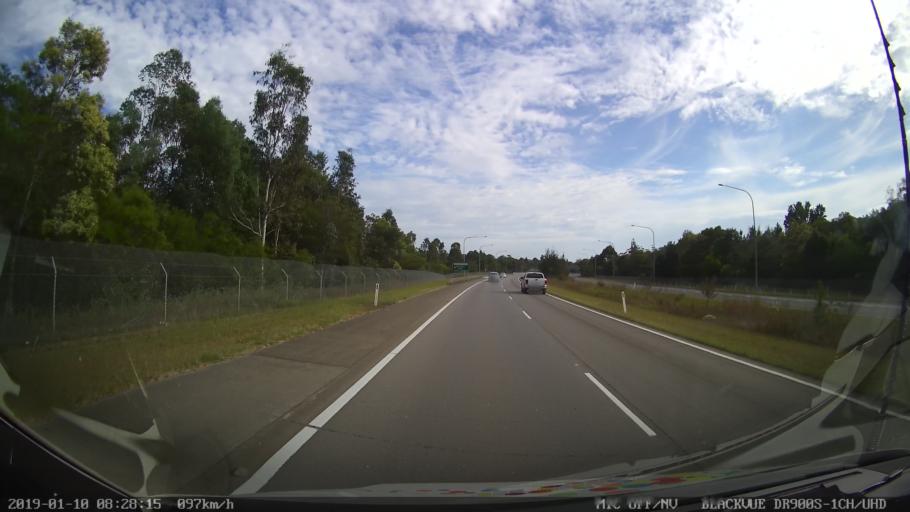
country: AU
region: New South Wales
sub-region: Coffs Harbour
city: Bonville
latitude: -30.3958
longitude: 153.0320
